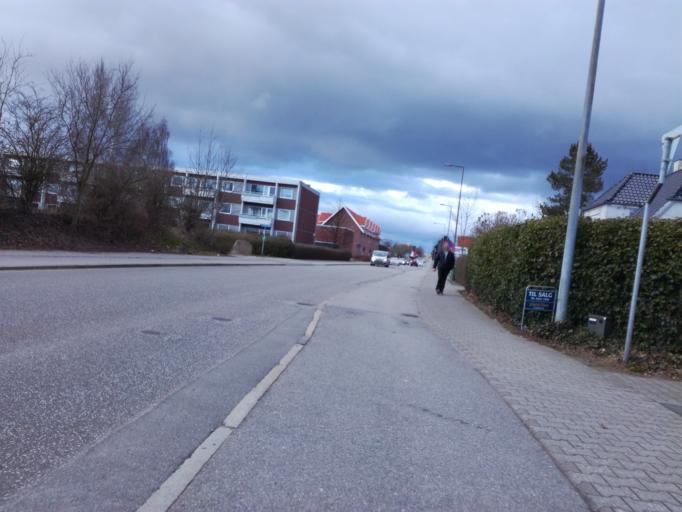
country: DK
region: South Denmark
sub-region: Fredericia Kommune
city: Fredericia
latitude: 55.5757
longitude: 9.7668
